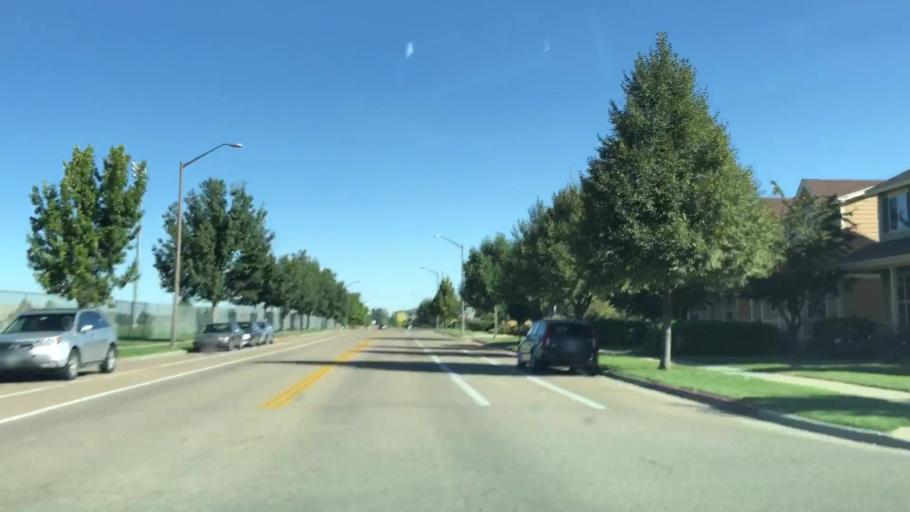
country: US
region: Colorado
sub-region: Larimer County
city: Fort Collins
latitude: 40.5131
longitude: -105.0104
